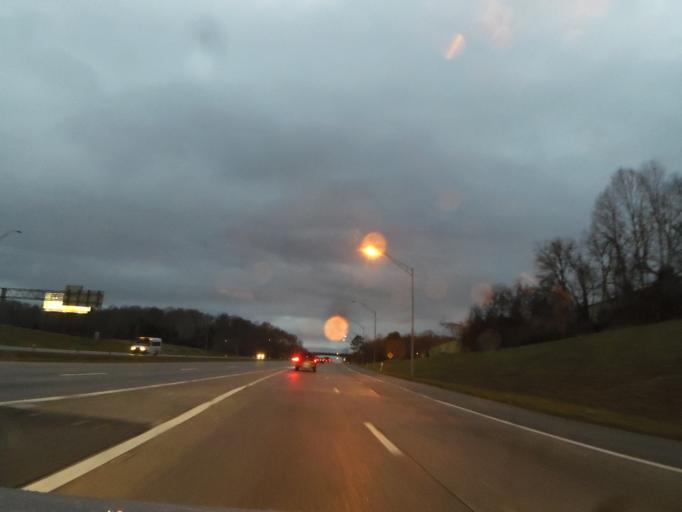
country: US
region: Tennessee
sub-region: Washington County
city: Oak Grove
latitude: 36.3572
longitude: -82.3994
